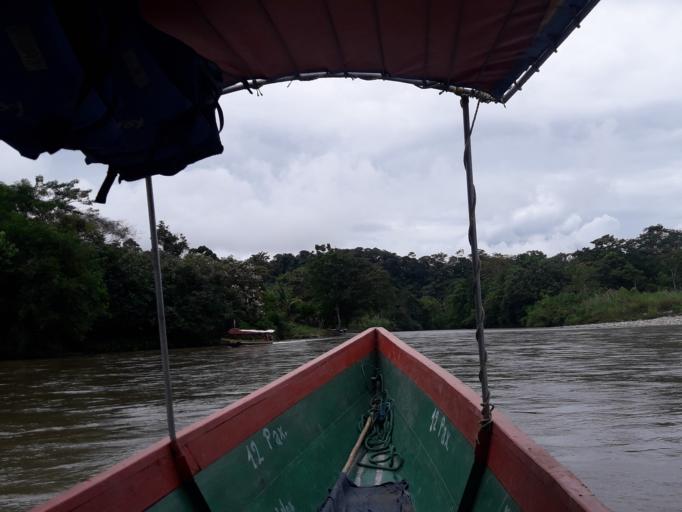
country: EC
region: Napo
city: Tena
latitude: -1.0364
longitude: -77.6578
